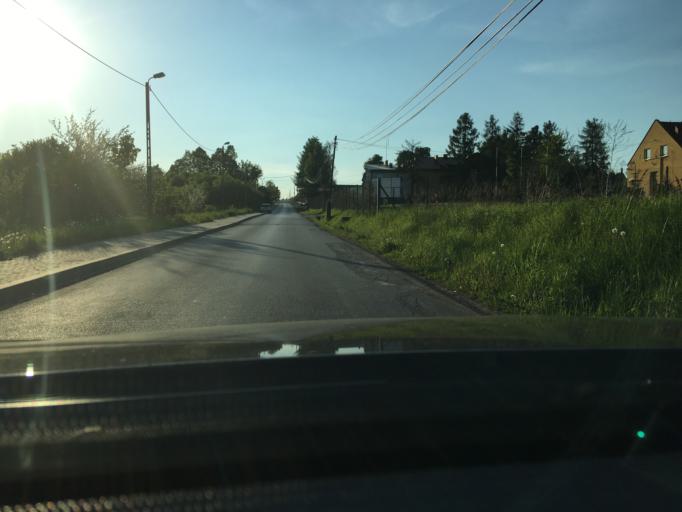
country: PL
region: Lesser Poland Voivodeship
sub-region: Powiat krakowski
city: Jerzmanowice
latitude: 50.2142
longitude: 19.7467
